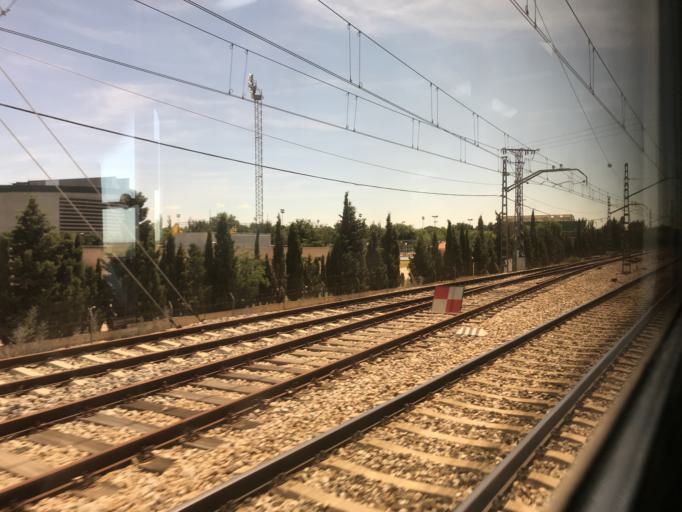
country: ES
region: Madrid
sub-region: Provincia de Madrid
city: Pinto
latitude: 40.2348
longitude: -3.7004
